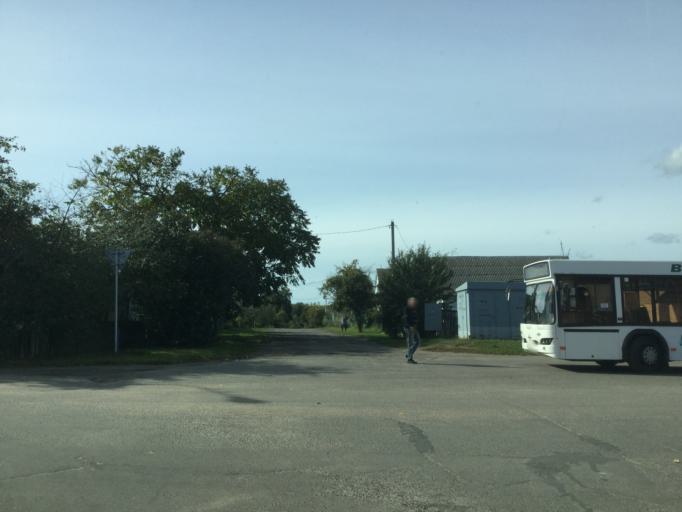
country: BY
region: Vitebsk
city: Horad Orsha
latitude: 54.5489
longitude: 30.4313
